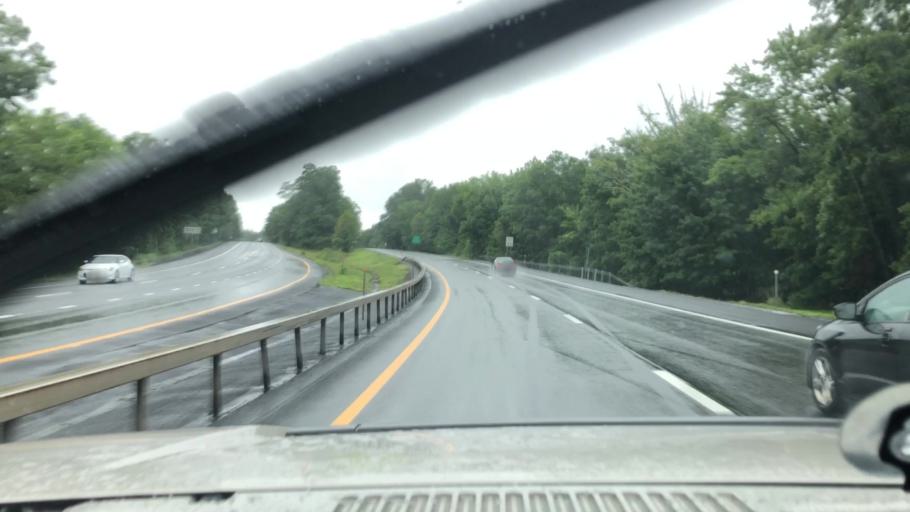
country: US
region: New York
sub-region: Greene County
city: Cairo
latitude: 42.3081
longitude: -74.0050
